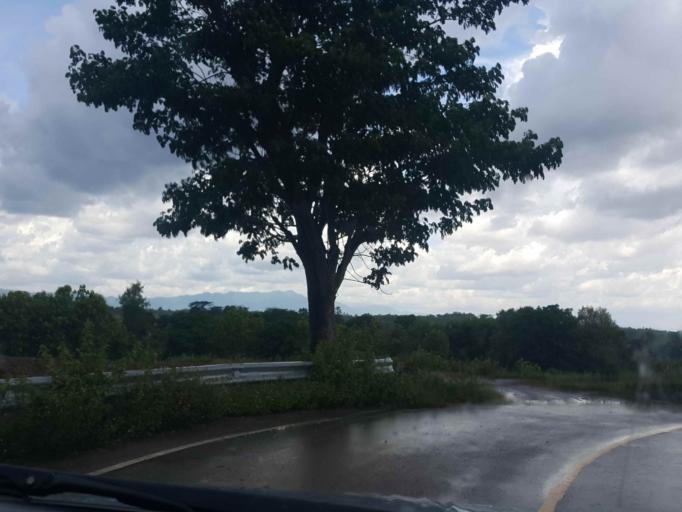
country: TH
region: Phayao
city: Dok Kham Tai
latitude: 19.0363
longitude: 99.9821
